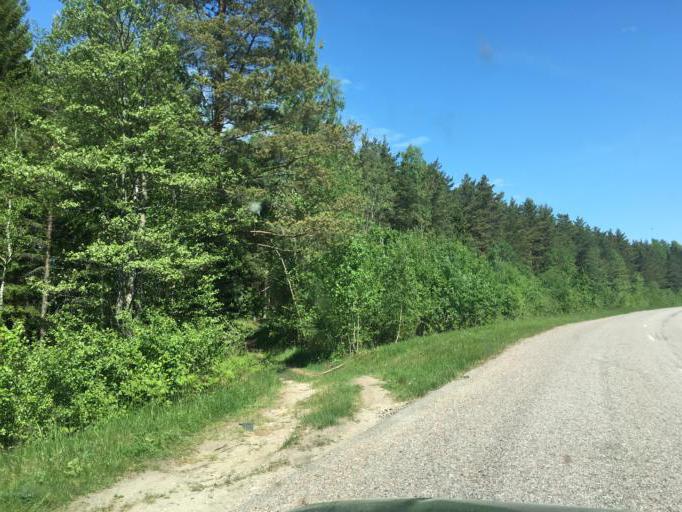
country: LV
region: Ventspils
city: Ventspils
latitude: 57.4646
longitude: 21.6534
